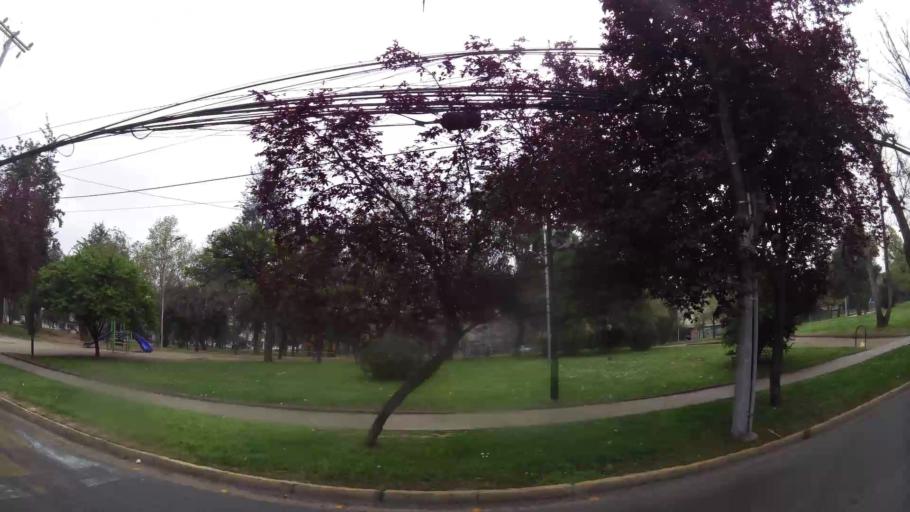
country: CL
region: Santiago Metropolitan
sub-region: Provincia de Santiago
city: Villa Presidente Frei, Nunoa, Santiago, Chile
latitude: -33.4702
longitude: -70.5894
